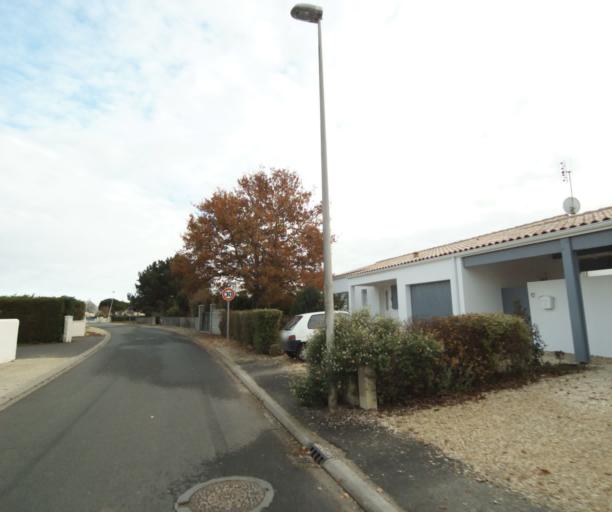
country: FR
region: Poitou-Charentes
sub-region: Departement de la Charente-Maritime
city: Corme-Royal
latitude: 45.7493
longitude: -0.8111
